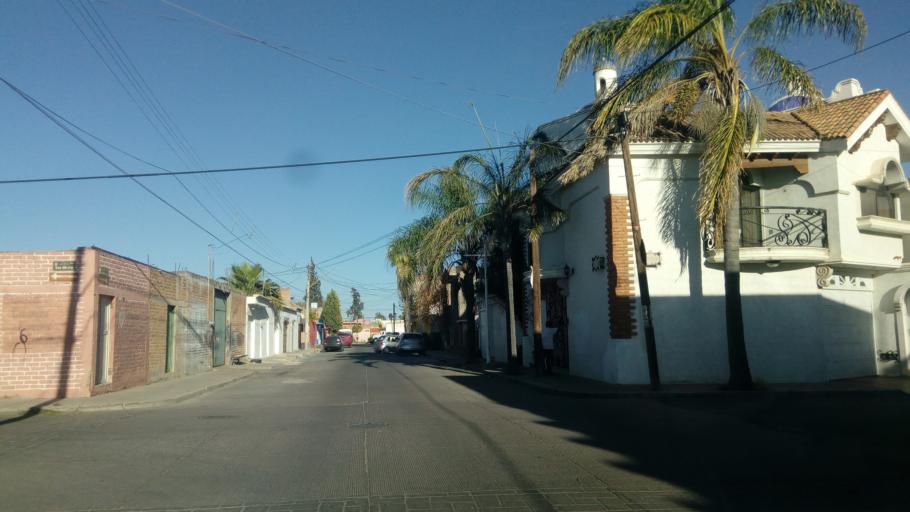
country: MX
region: Durango
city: Victoria de Durango
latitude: 24.0114
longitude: -104.6794
